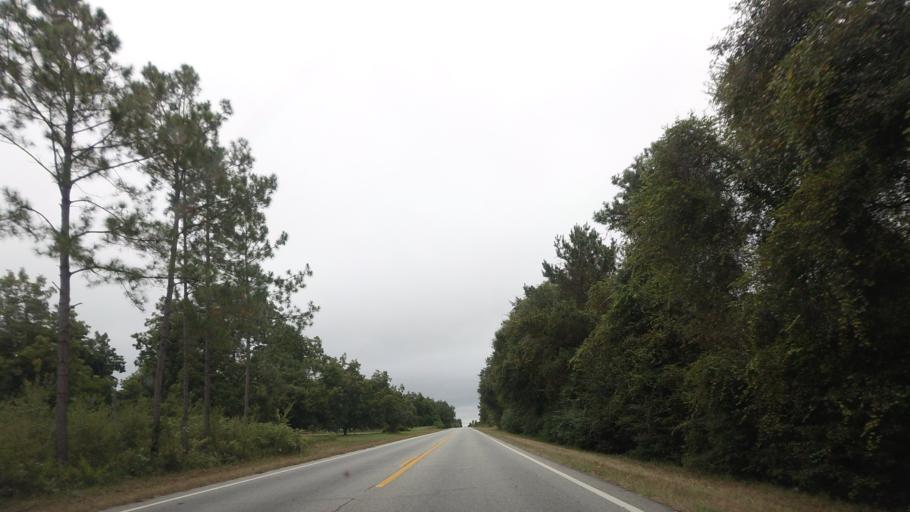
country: US
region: Georgia
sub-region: Berrien County
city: Ray City
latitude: 31.1083
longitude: -83.2097
